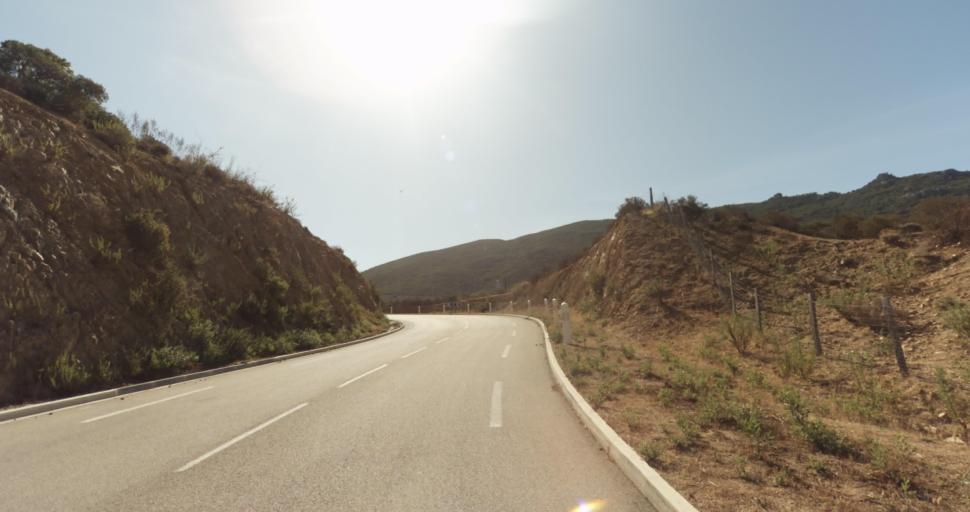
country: FR
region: Corsica
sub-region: Departement de la Corse-du-Sud
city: Ajaccio
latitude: 41.9330
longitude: 8.6718
